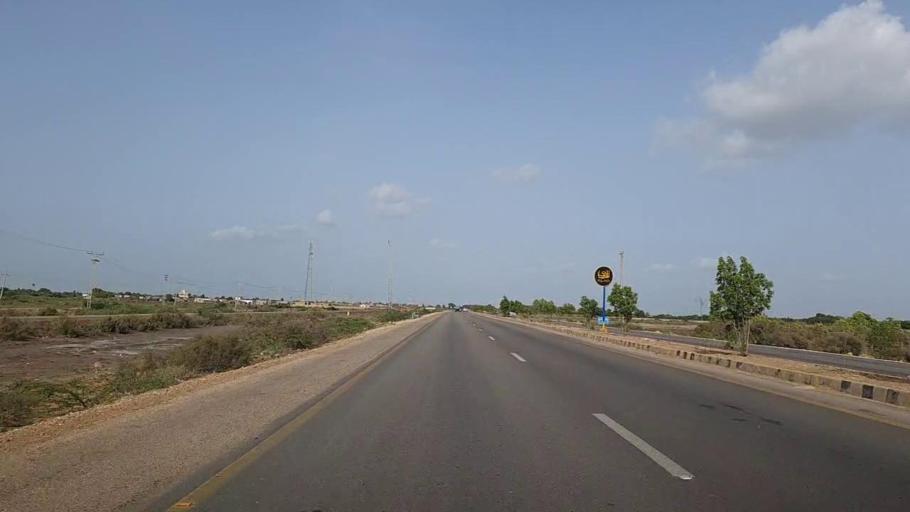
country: PK
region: Sindh
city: Gharo
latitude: 24.7397
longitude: 67.7484
